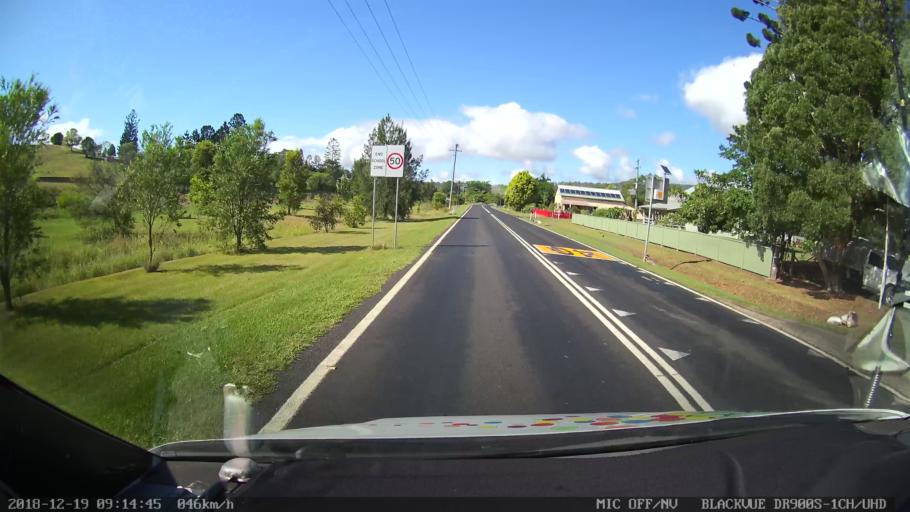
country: AU
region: New South Wales
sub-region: Kyogle
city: Kyogle
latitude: -28.5091
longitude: 152.9653
